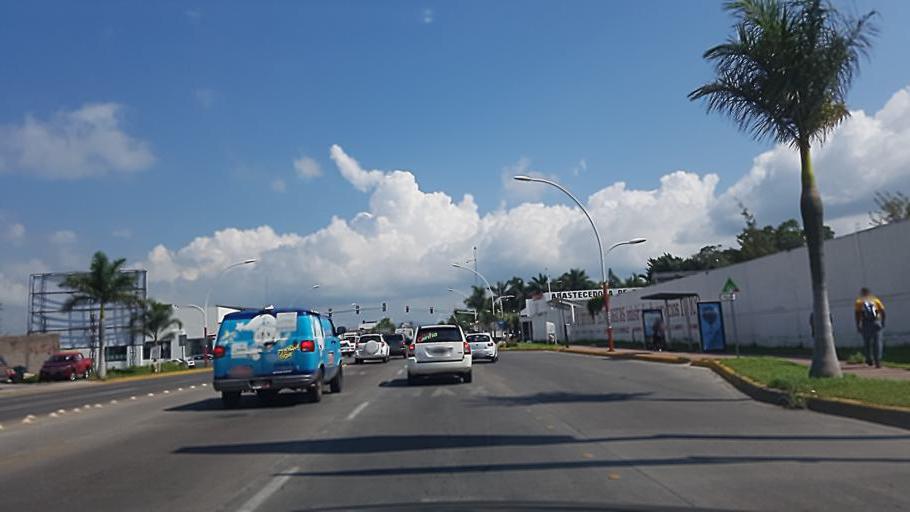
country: MX
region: Nayarit
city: Xalisco
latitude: 21.4797
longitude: -104.8918
